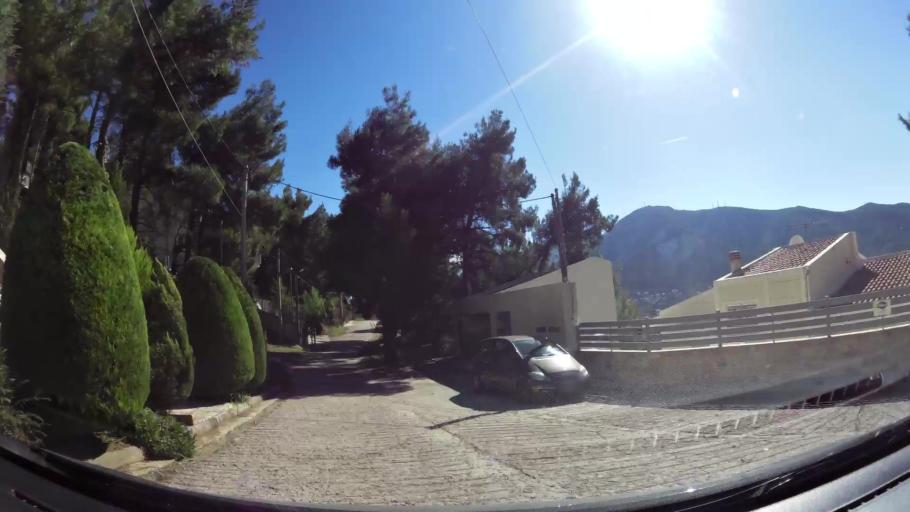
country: GR
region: Attica
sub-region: Nomarchia Anatolikis Attikis
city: Dionysos
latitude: 38.1073
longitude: 23.8896
